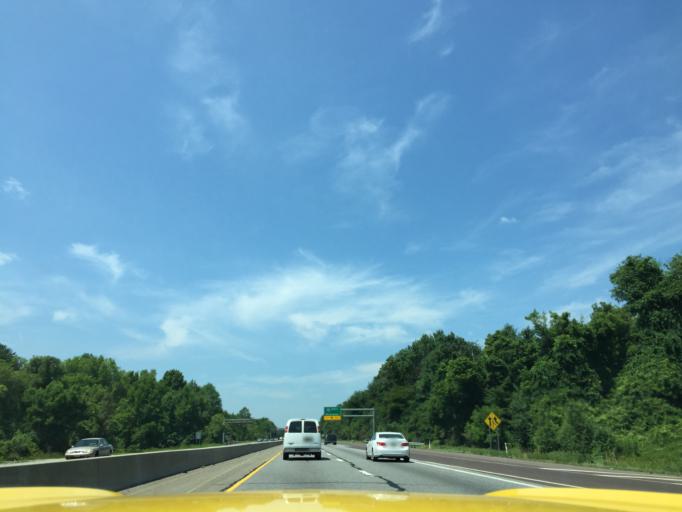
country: US
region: Pennsylvania
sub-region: Bucks County
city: Fairless Hills
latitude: 40.1934
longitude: -74.8675
